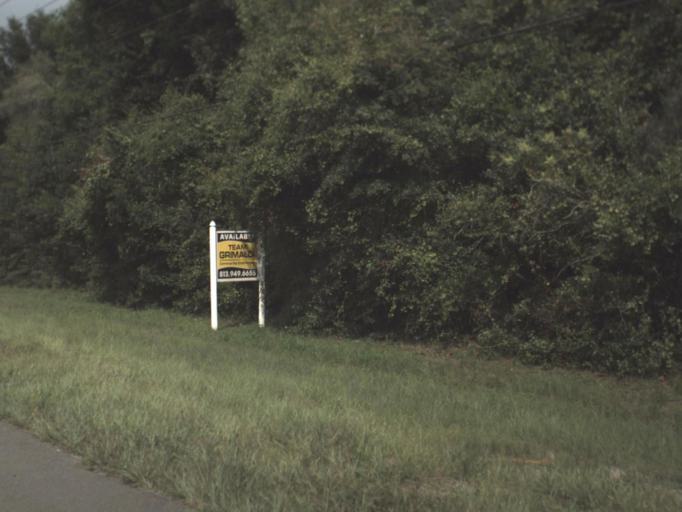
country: US
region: Florida
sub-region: Pasco County
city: Shady Hills
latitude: 28.3705
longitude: -82.4949
